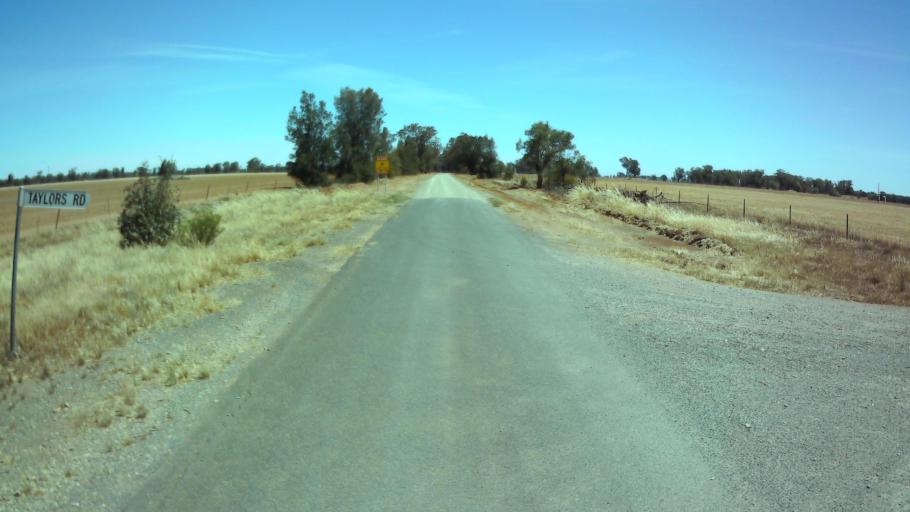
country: AU
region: New South Wales
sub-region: Weddin
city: Grenfell
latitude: -33.9065
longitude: 147.6853
